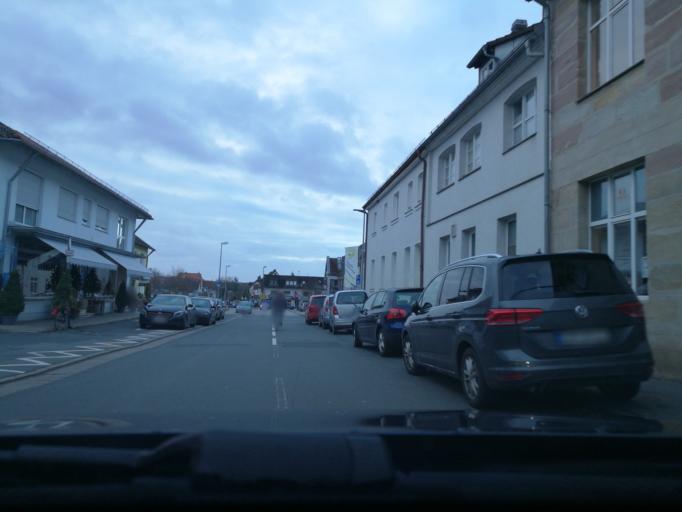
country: DE
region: Bavaria
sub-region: Regierungsbezirk Mittelfranken
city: Uttenreuth
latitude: 49.5981
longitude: 11.0744
